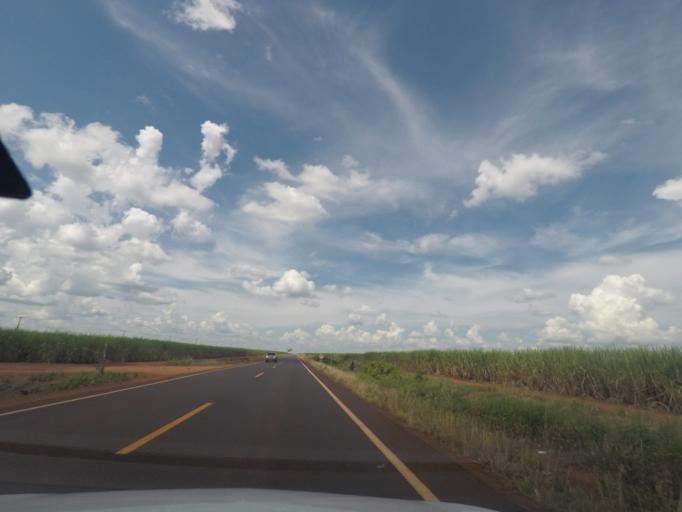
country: BR
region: Minas Gerais
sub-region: Conceicao Das Alagoas
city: Conceicao das Alagoas
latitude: -19.8670
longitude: -48.6133
